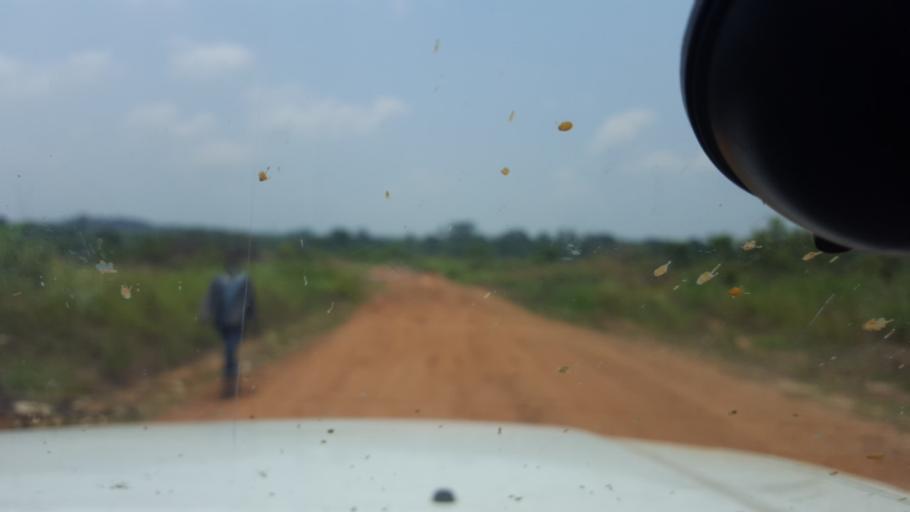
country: CD
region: Bandundu
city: Mushie
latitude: -3.7449
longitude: 16.6557
